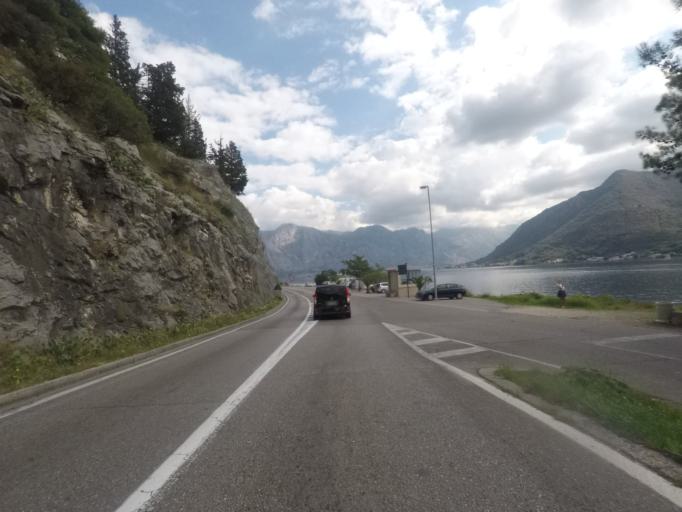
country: ME
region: Kotor
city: Risan
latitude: 42.4843
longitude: 18.7073
